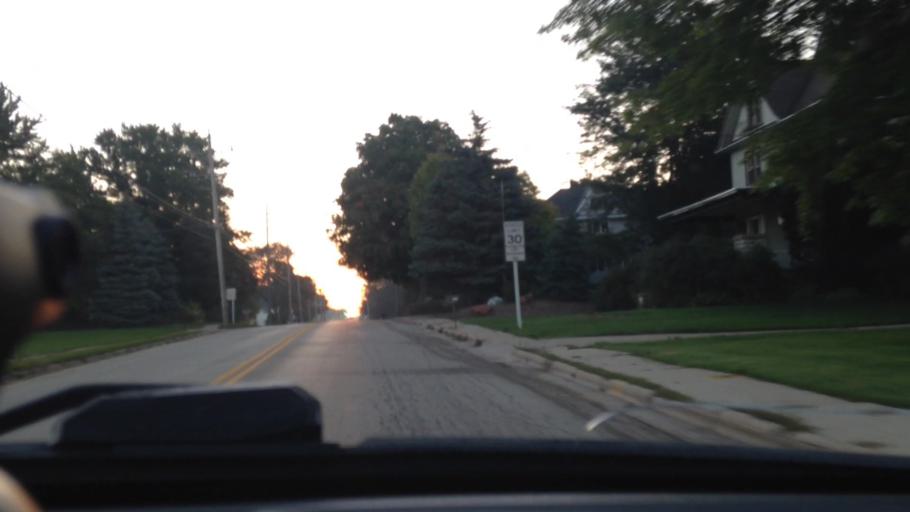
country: US
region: Wisconsin
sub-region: Dodge County
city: Lomira
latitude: 43.5871
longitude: -88.4398
